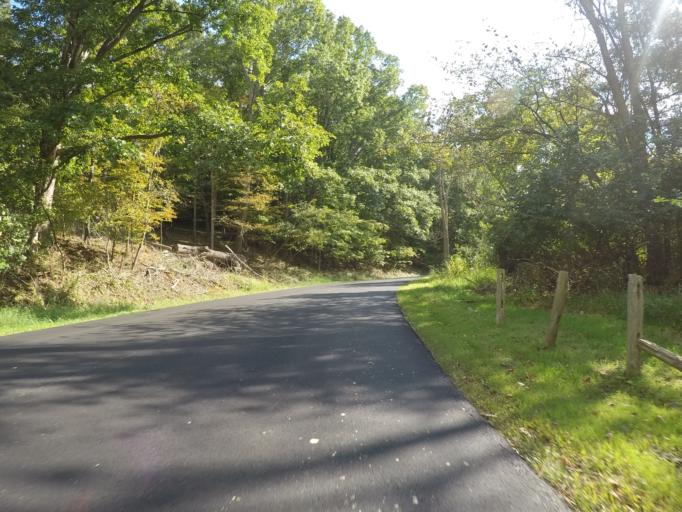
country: US
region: West Virginia
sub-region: Cabell County
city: Huntington
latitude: 38.3899
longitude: -82.4272
